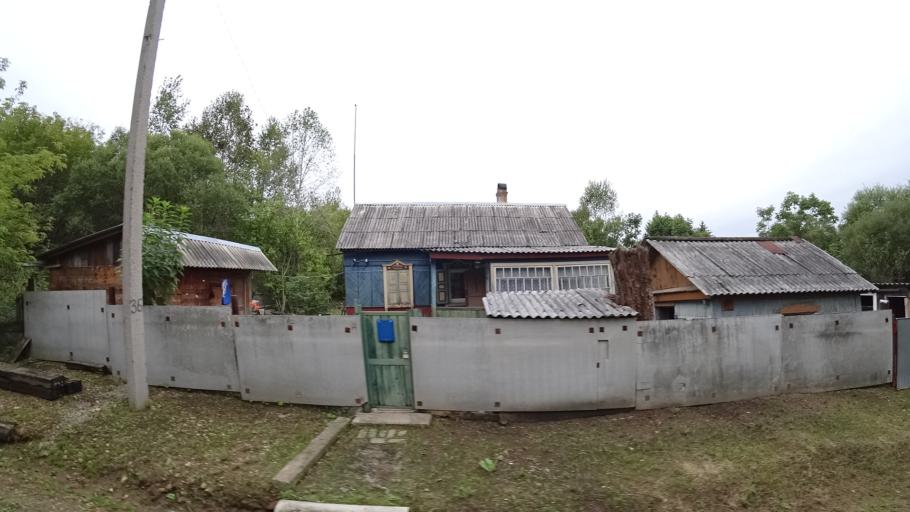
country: RU
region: Primorskiy
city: Rettikhovka
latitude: 44.1604
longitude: 132.7433
